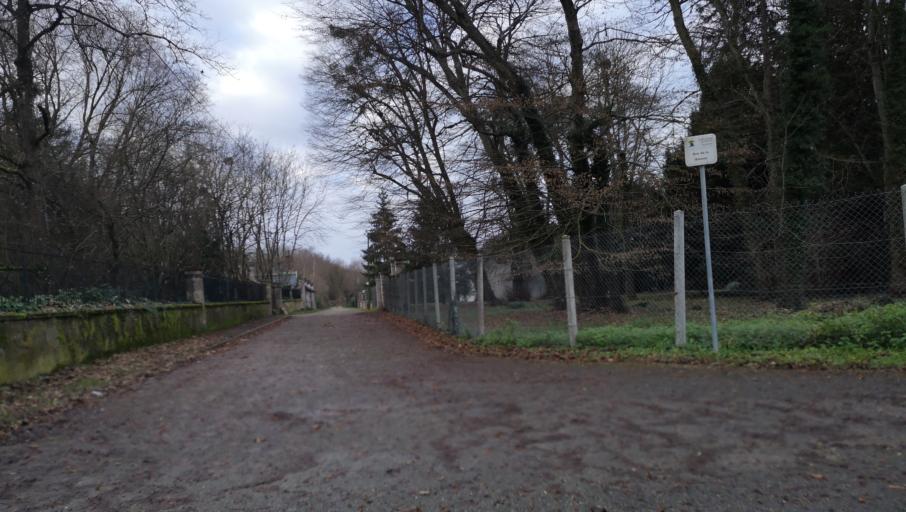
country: FR
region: Centre
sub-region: Departement du Loiret
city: Boigny-sur-Bionne
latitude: 47.9177
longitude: 2.0039
